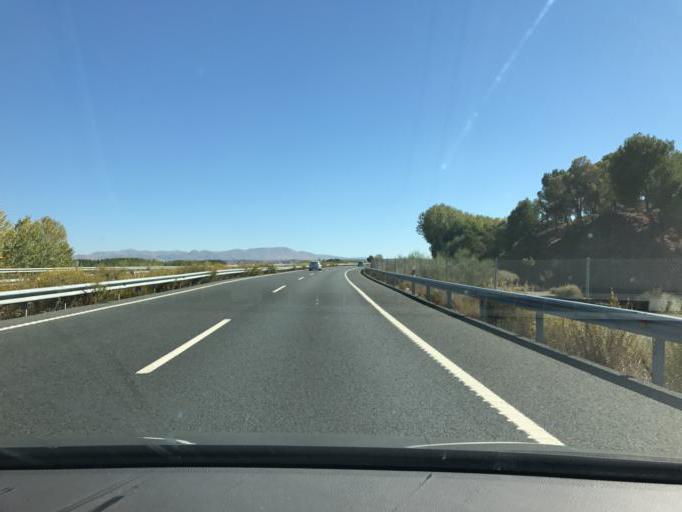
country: ES
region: Andalusia
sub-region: Provincia de Granada
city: Purullena
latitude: 37.3284
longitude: -3.1824
